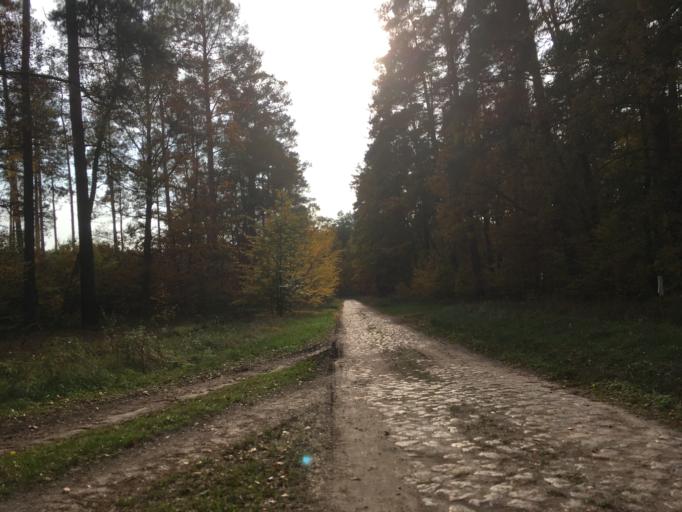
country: DE
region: Brandenburg
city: Liebenwalde
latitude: 52.9623
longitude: 13.4844
